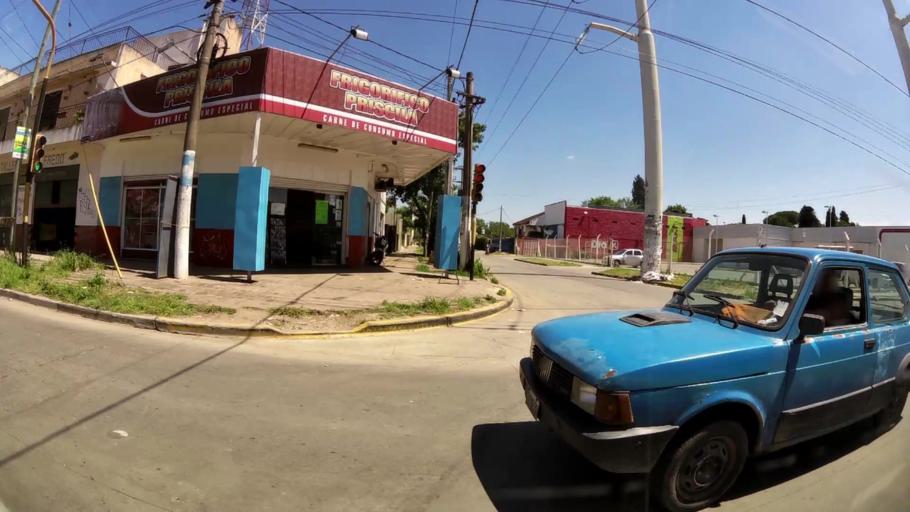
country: AR
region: Buenos Aires
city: Ituzaingo
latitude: -34.6798
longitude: -58.6709
